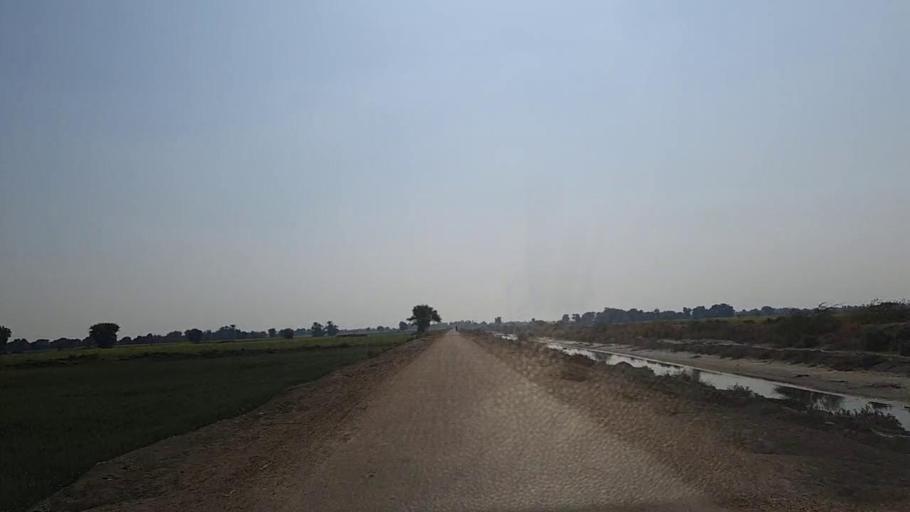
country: PK
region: Sindh
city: Nawabshah
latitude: 26.2605
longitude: 68.5031
